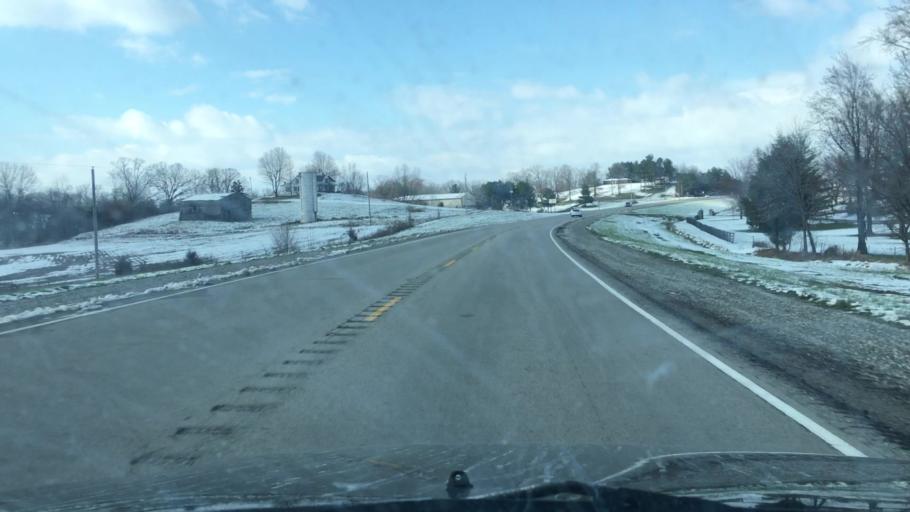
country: US
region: Kentucky
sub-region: Marion County
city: Lebanon
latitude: 37.5352
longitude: -85.3056
